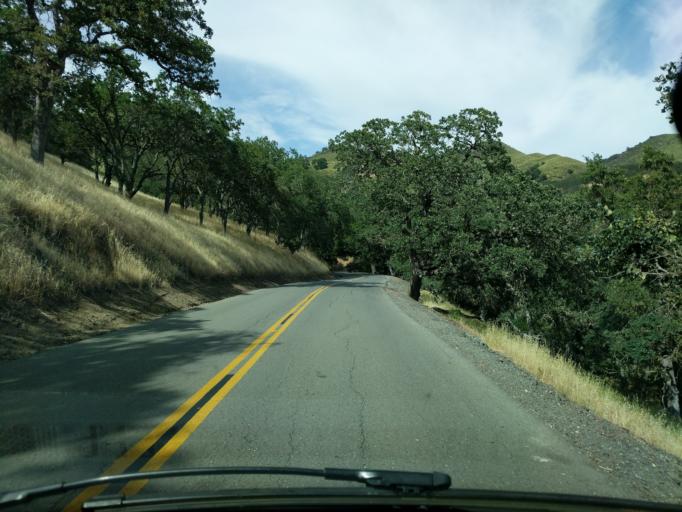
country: US
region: California
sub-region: Contra Costa County
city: Diablo
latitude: 37.8423
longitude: -121.9432
